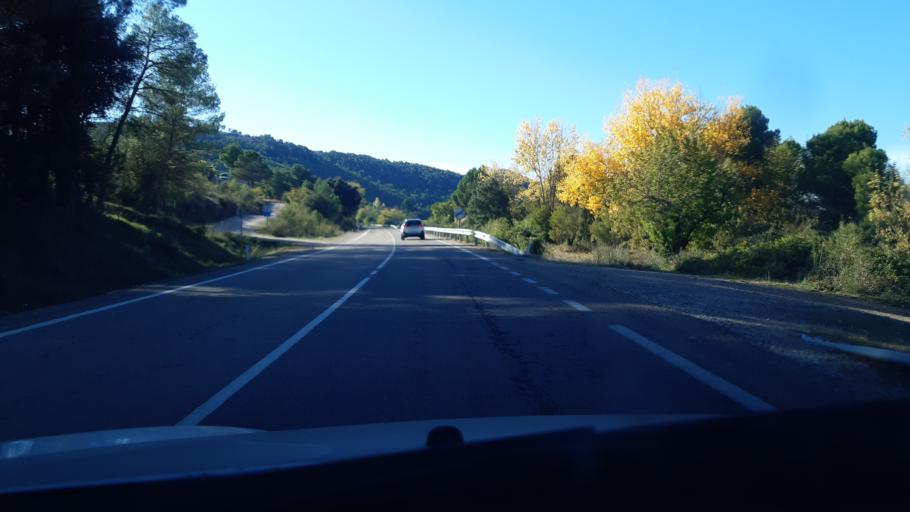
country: ES
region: Aragon
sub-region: Provincia de Teruel
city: Valderrobres
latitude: 40.8827
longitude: 0.1291
